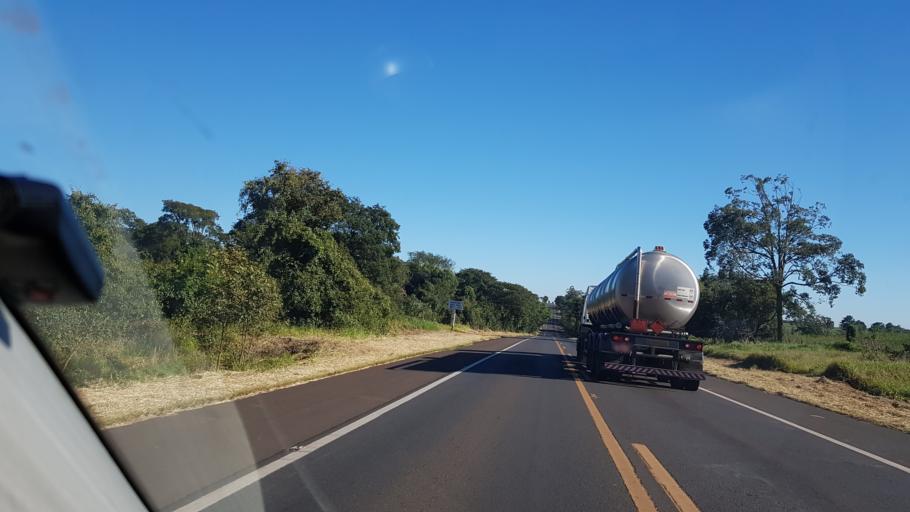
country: BR
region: Sao Paulo
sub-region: Assis
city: Assis
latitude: -22.5825
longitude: -50.5040
